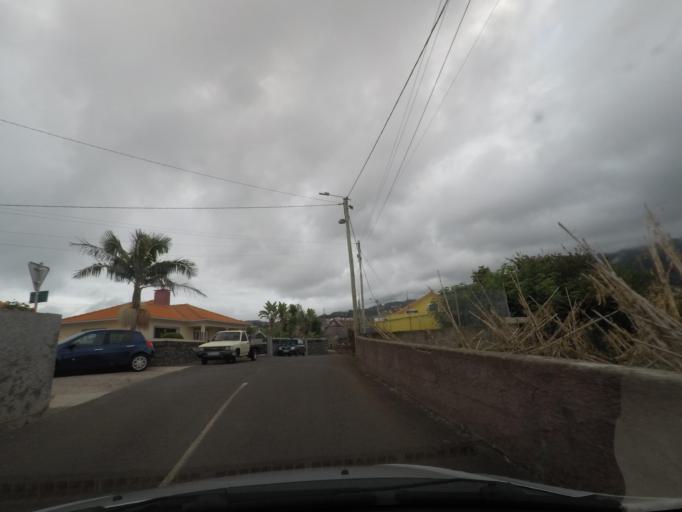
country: PT
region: Madeira
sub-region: Santana
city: Santana
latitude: 32.8165
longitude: -16.8845
